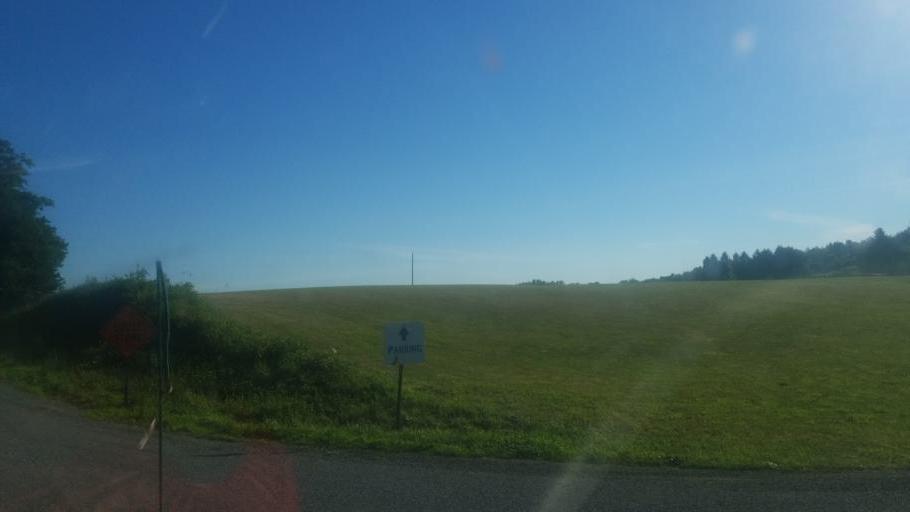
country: US
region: New York
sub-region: Wayne County
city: Lyons
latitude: 43.0788
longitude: -77.0286
